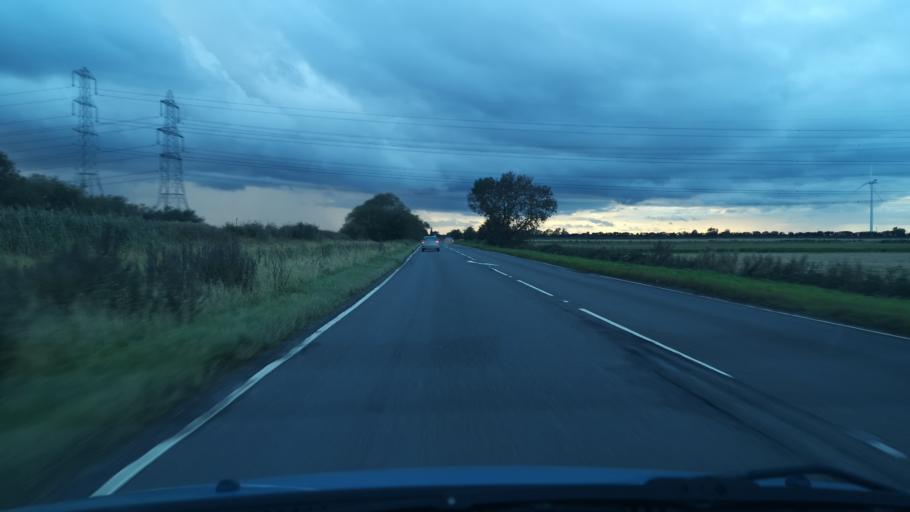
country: GB
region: England
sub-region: North Lincolnshire
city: Gunness
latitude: 53.5770
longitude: -0.7578
